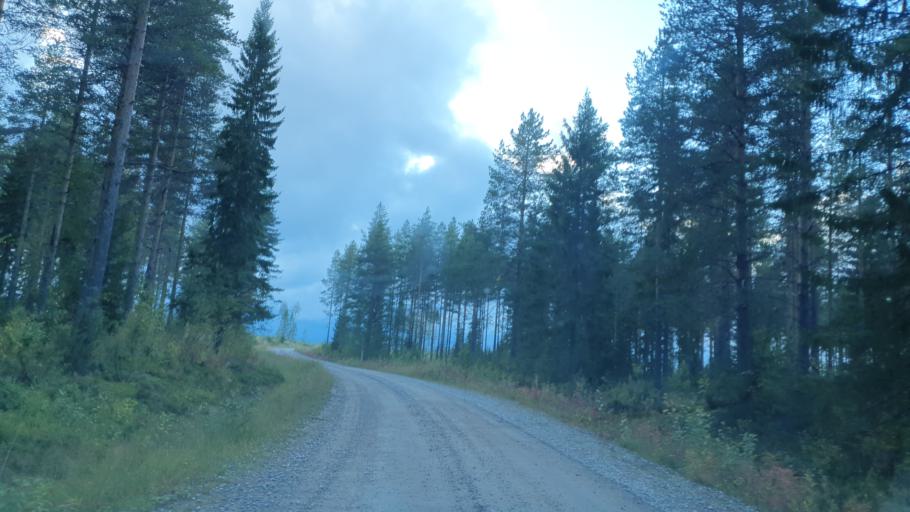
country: FI
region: Kainuu
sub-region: Kehys-Kainuu
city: Kuhmo
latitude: 64.3367
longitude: 29.9124
